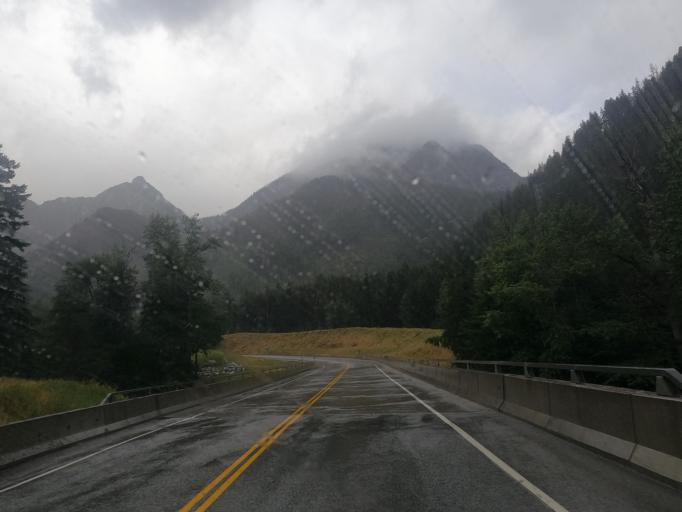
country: CA
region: British Columbia
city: Lillooet
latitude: 50.5338
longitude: -122.1499
